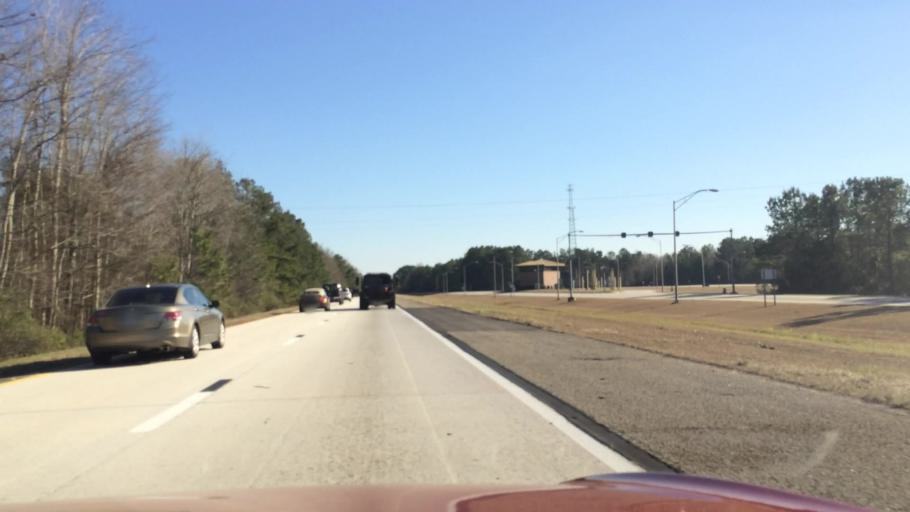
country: US
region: South Carolina
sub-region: Orangeburg County
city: Holly Hill
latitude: 33.2710
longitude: -80.4893
